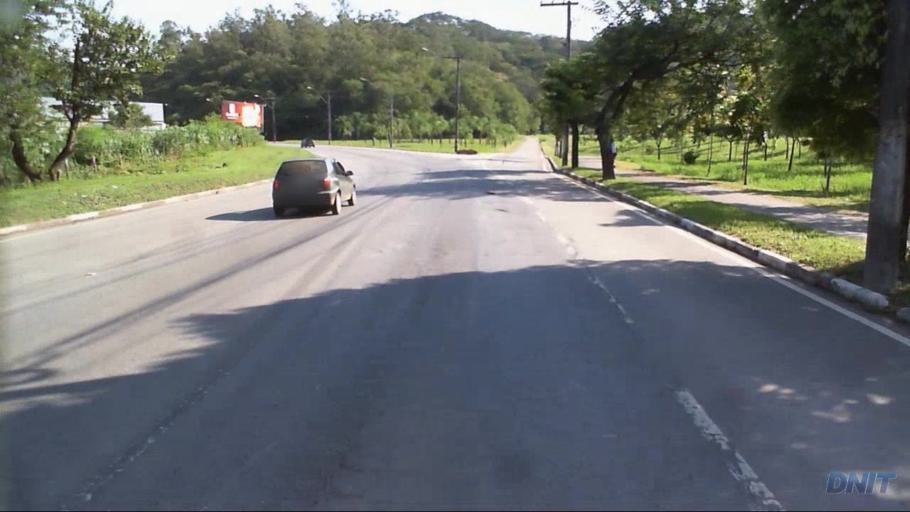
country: BR
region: Minas Gerais
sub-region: Ipatinga
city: Ipatinga
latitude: -19.4910
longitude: -42.5628
